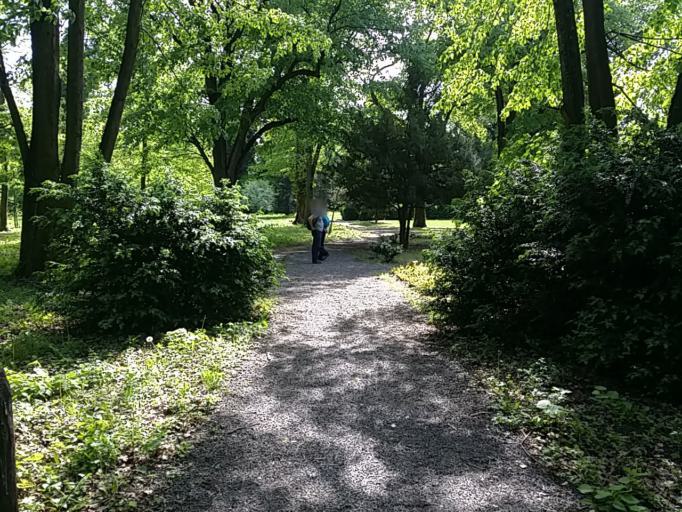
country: HU
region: Bekes
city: Doboz
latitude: 46.6889
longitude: 21.1954
